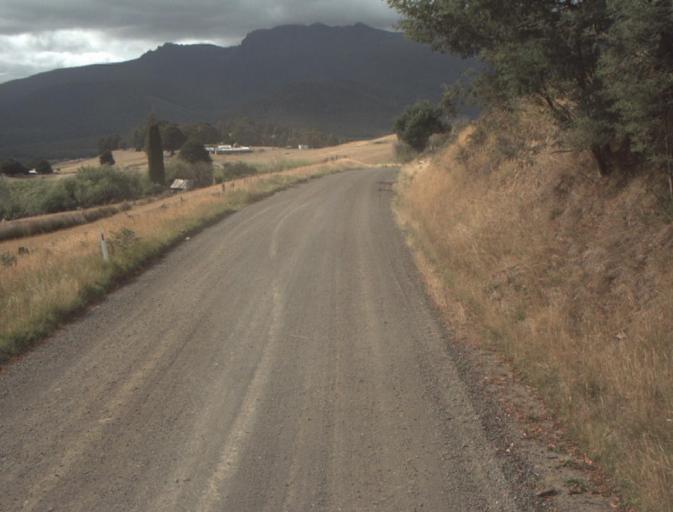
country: AU
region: Tasmania
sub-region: Dorset
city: Scottsdale
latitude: -41.4471
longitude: 147.5864
